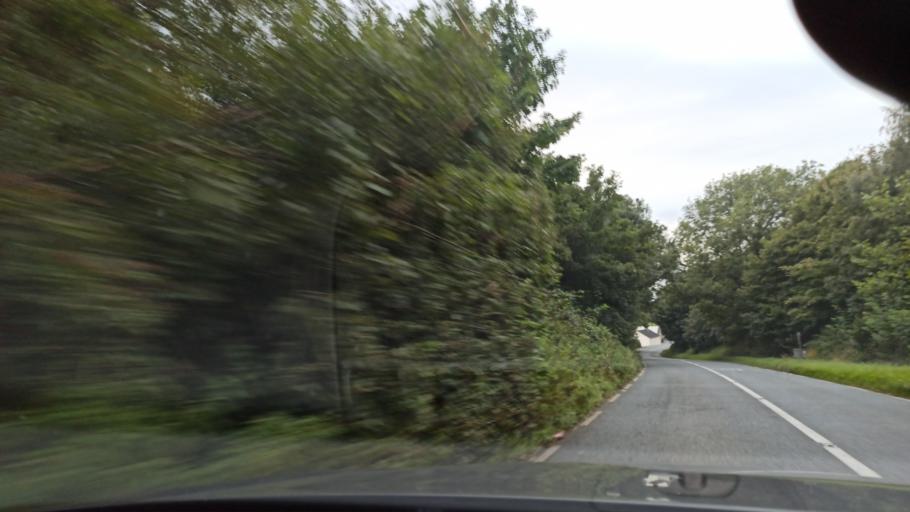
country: IE
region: Munster
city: Cashel
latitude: 52.4759
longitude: -7.8490
